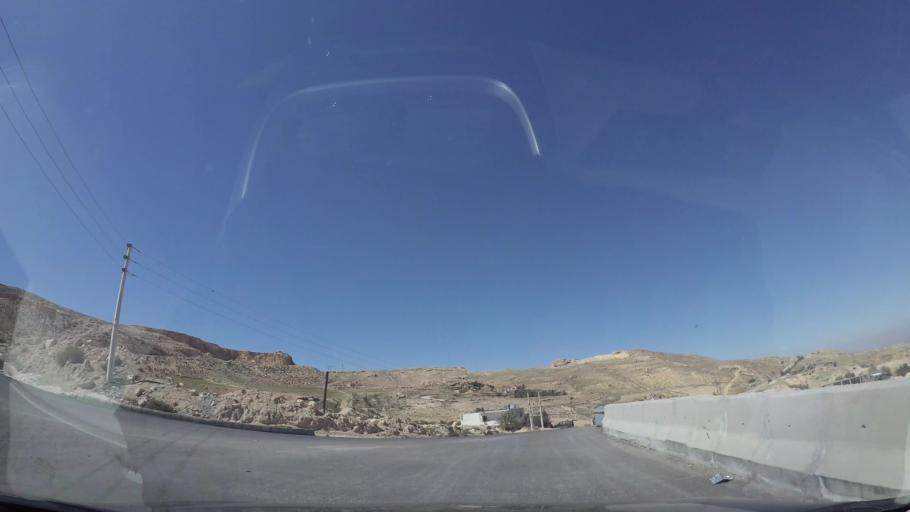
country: JO
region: Tafielah
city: At Tafilah
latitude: 30.8407
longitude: 35.5644
